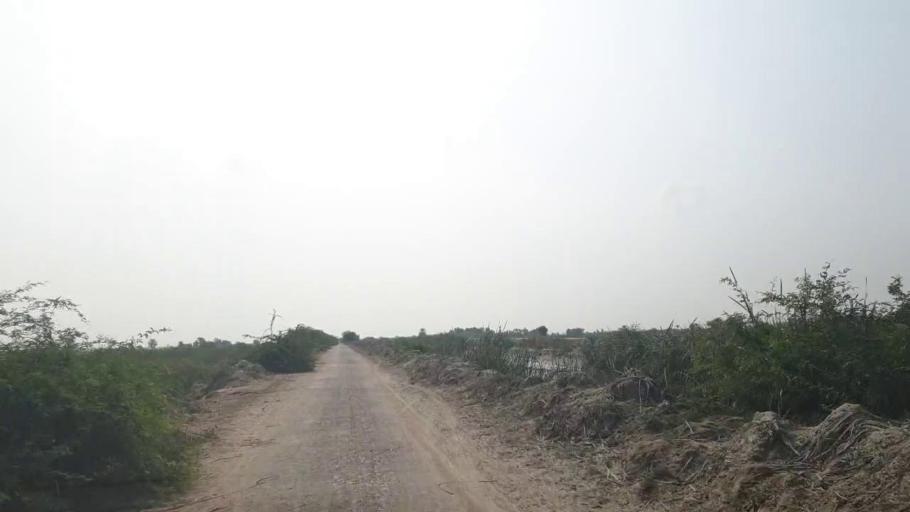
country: PK
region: Sindh
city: Badin
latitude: 24.7238
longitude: 68.7347
